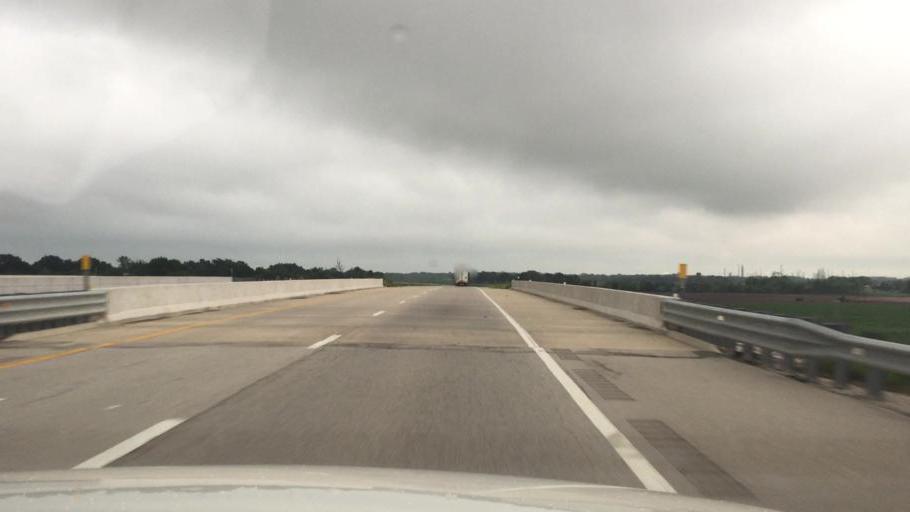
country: US
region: Kansas
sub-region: Montgomery County
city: Coffeyville
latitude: 37.0870
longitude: -95.5898
